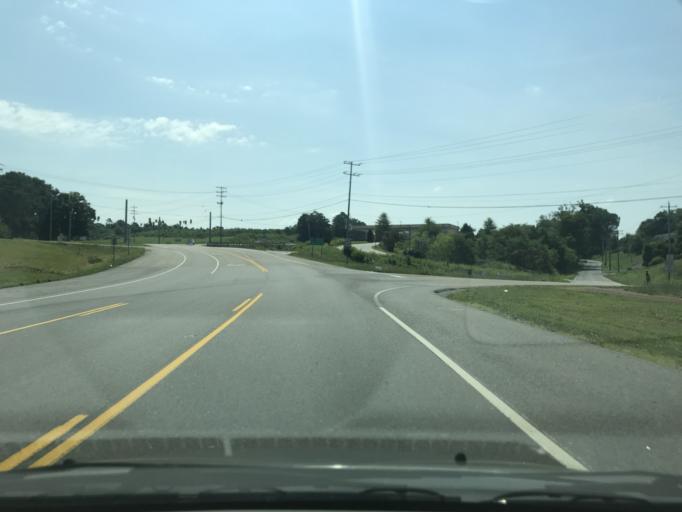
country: US
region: Tennessee
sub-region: Loudon County
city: Lenoir City
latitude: 35.8367
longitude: -84.2942
